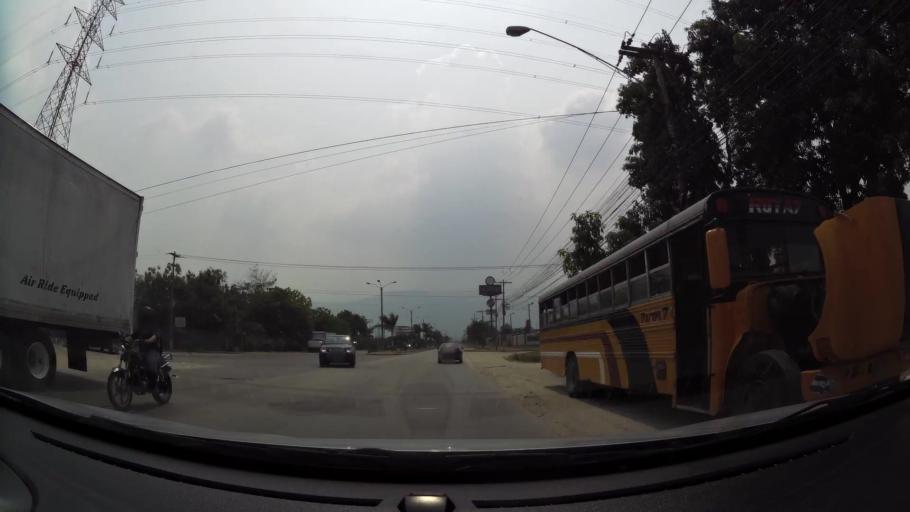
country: HN
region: Cortes
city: San Pedro Sula
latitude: 15.4717
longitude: -88.0028
